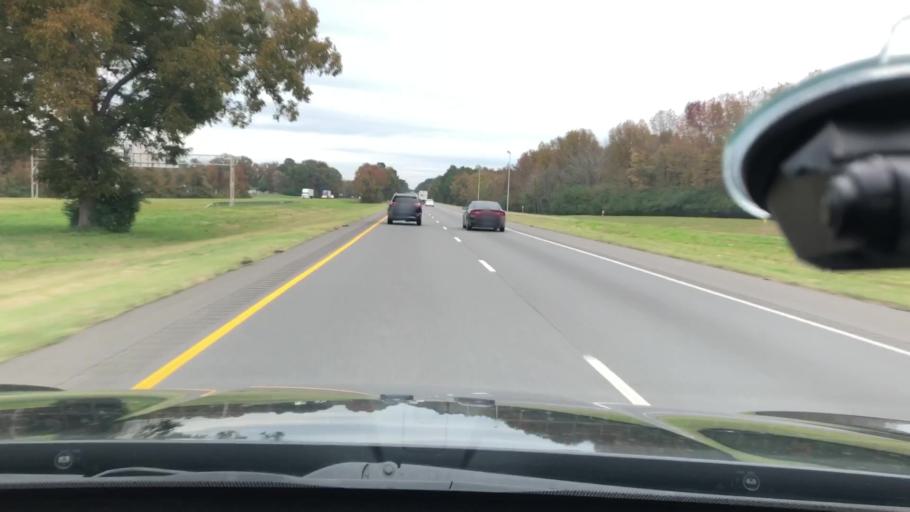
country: US
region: Arkansas
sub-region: Hempstead County
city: Hope
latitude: 33.6926
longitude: -93.5957
